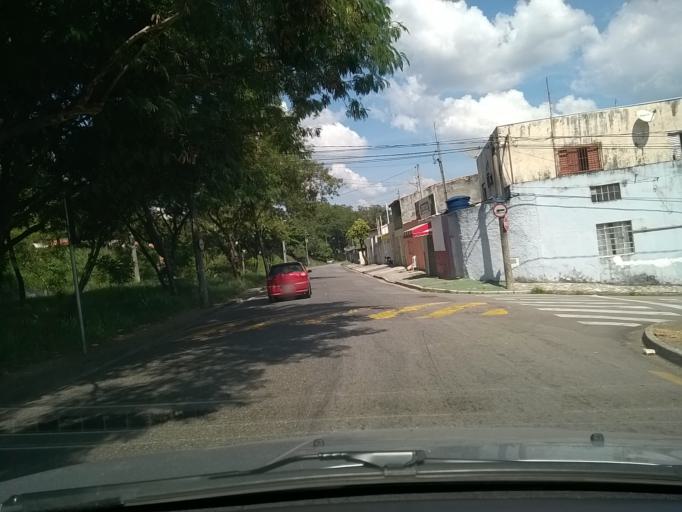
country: BR
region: Sao Paulo
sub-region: Jundiai
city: Jundiai
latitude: -23.2151
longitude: -46.8727
